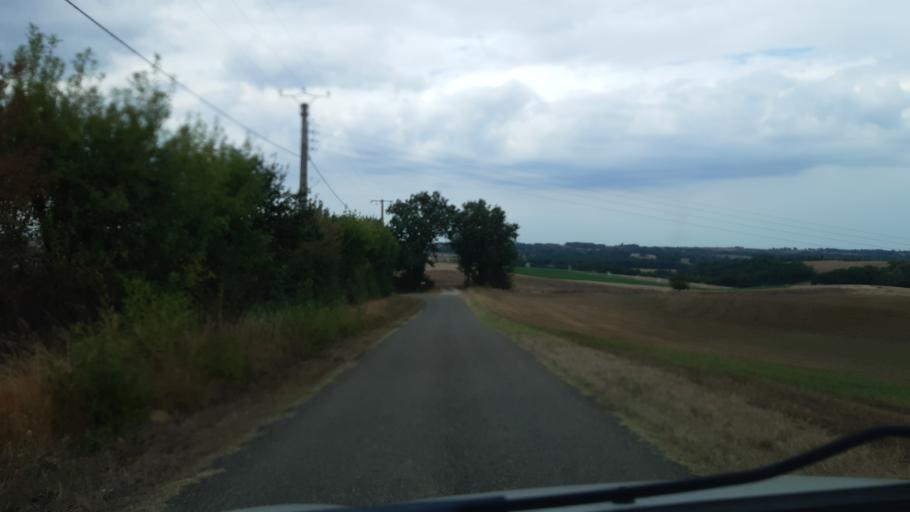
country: FR
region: Midi-Pyrenees
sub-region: Departement du Gers
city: Gimont
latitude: 43.7007
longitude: 0.9894
